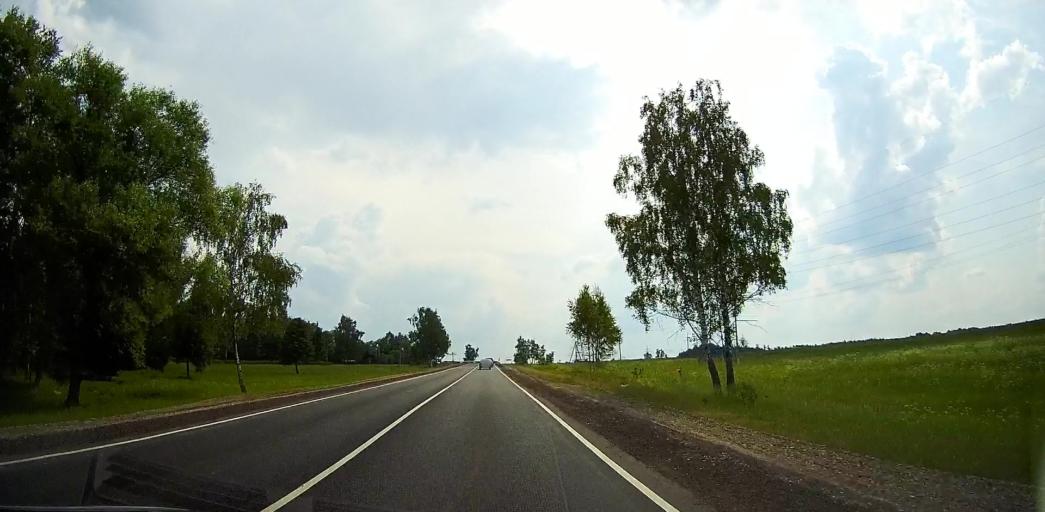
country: RU
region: Moskovskaya
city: Stupino
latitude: 54.9396
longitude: 38.1340
